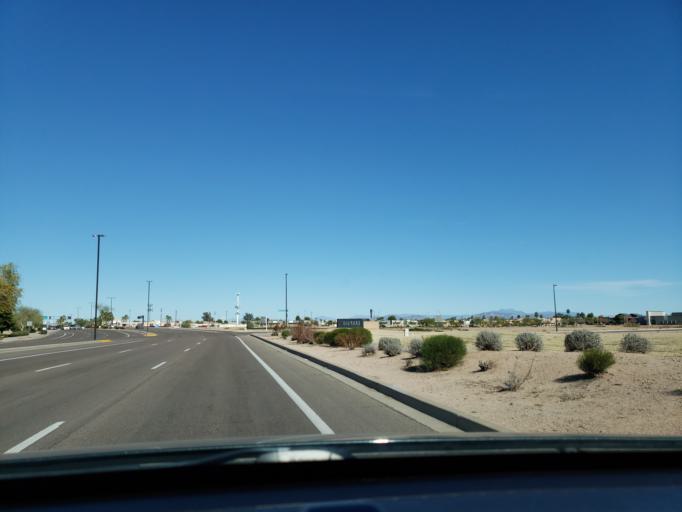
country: US
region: Arizona
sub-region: Maricopa County
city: Gilbert
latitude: 33.3325
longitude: -111.7902
